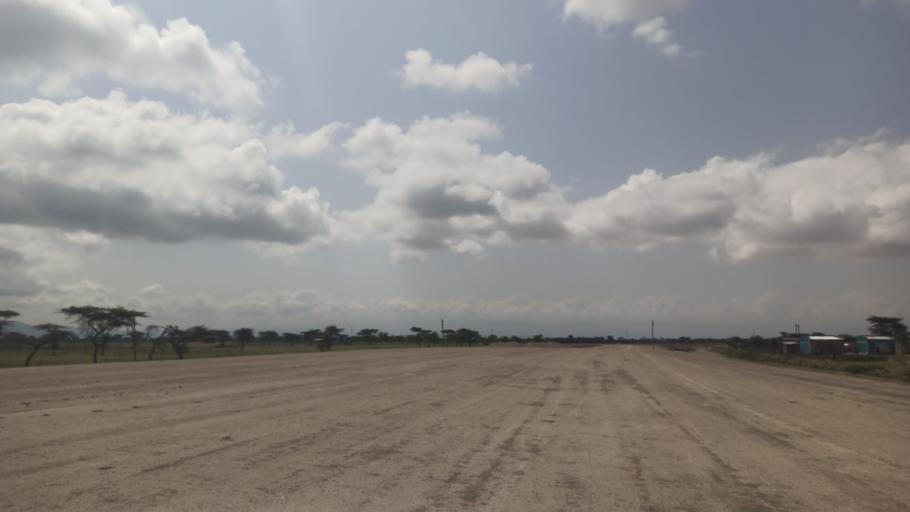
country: ET
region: Oromiya
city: Ziway
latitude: 7.6905
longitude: 38.6607
